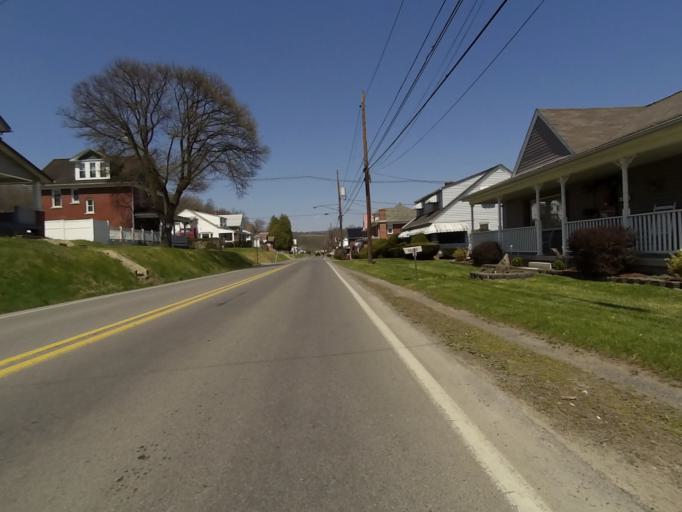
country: US
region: Pennsylvania
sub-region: Blair County
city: Williamsburg
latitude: 40.4653
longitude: -78.1992
